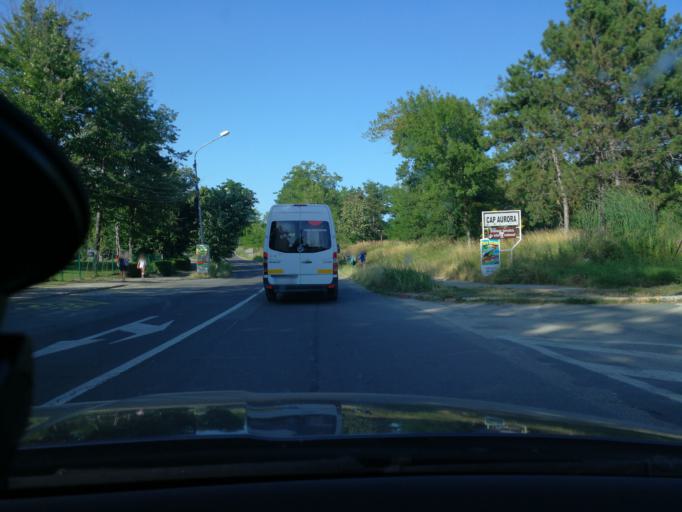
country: RO
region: Constanta
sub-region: Municipiul Mangalia
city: Mangalia
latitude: 43.8488
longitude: 28.5999
